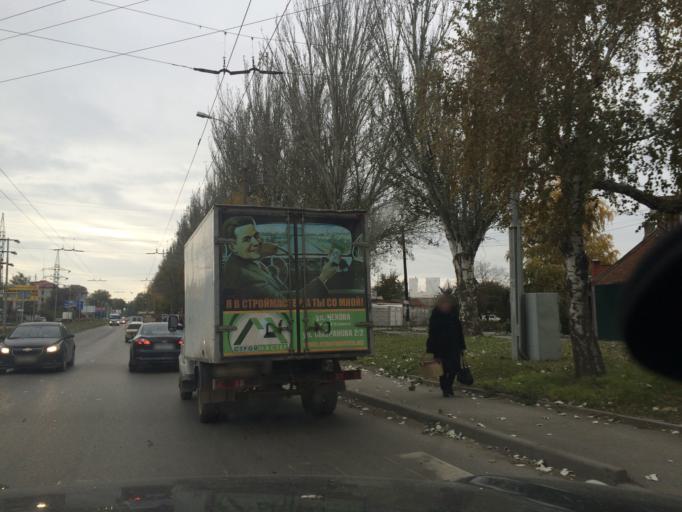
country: RU
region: Rostov
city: Taganrog
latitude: 47.2461
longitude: 38.9177
